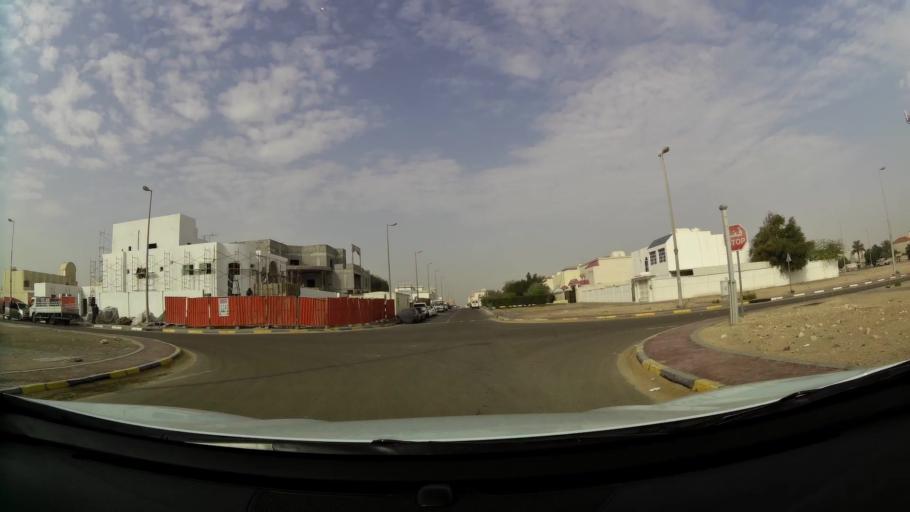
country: AE
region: Abu Dhabi
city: Abu Dhabi
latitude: 24.2541
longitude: 54.7221
